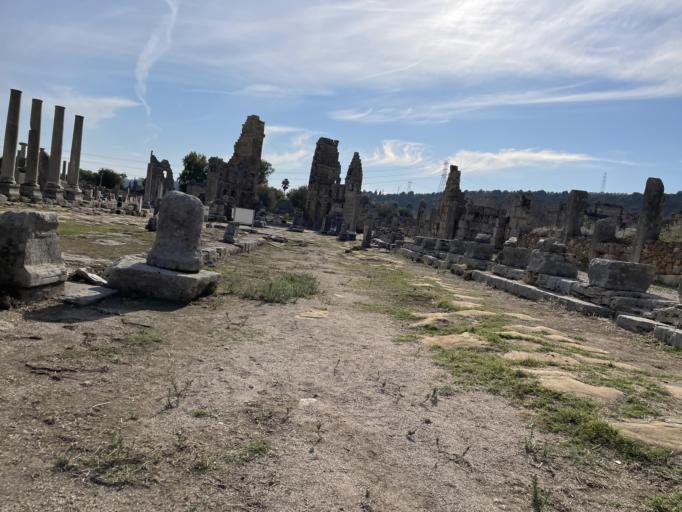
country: TR
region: Antalya
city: Aksu
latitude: 36.9623
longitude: 30.8544
